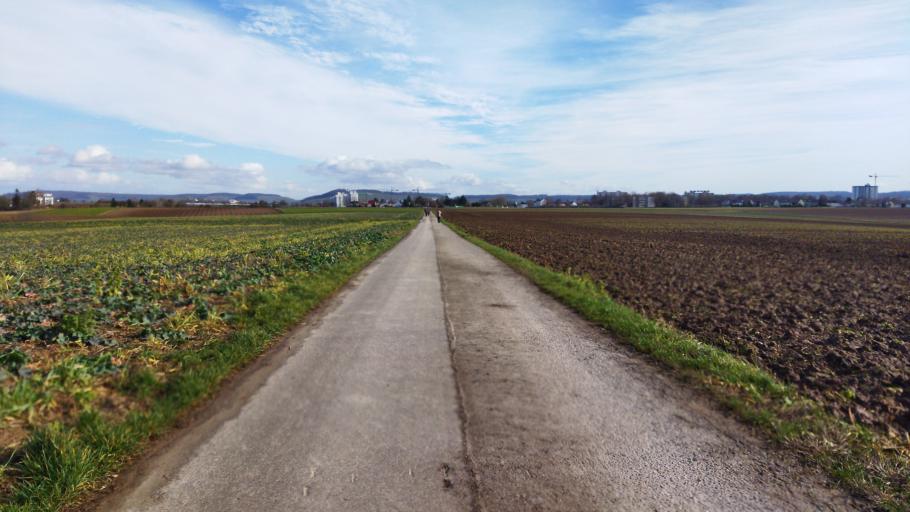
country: DE
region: Baden-Wuerttemberg
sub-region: Regierungsbezirk Stuttgart
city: Leingarten
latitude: 49.1519
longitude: 9.1658
